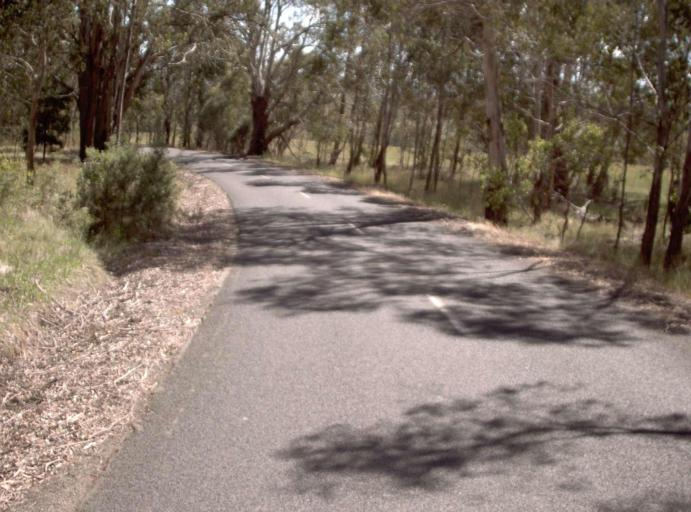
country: AU
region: New South Wales
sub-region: Bombala
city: Bombala
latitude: -37.0565
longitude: 148.8051
